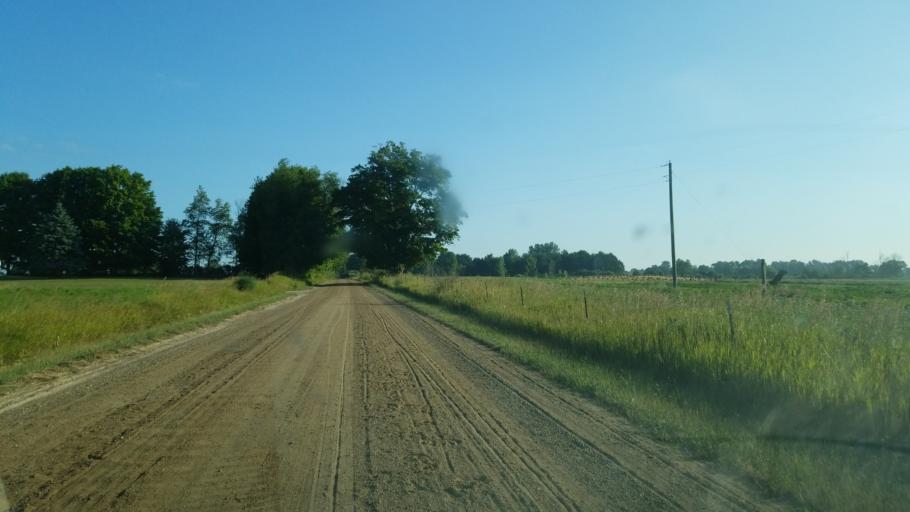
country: US
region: Michigan
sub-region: Mecosta County
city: Canadian Lakes
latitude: 43.5507
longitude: -85.3632
